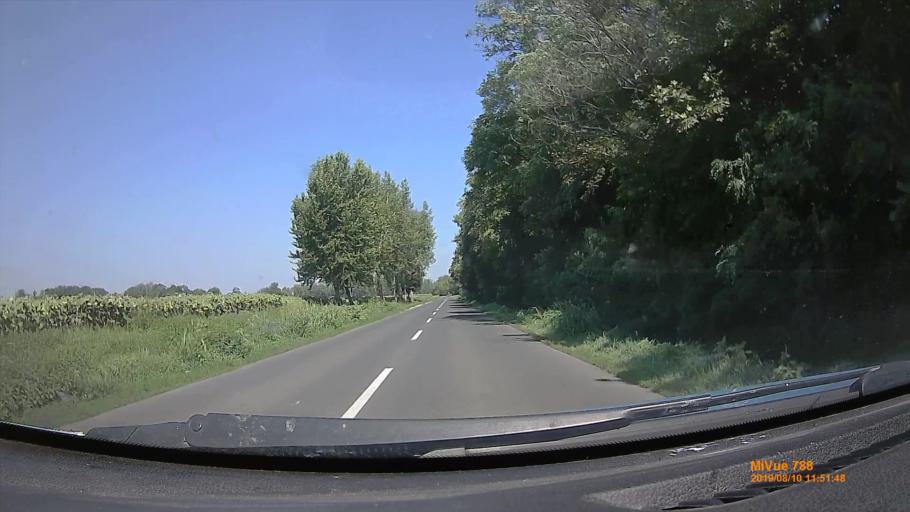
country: HU
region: Somogy
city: Somogyvar
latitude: 46.4978
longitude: 17.7133
